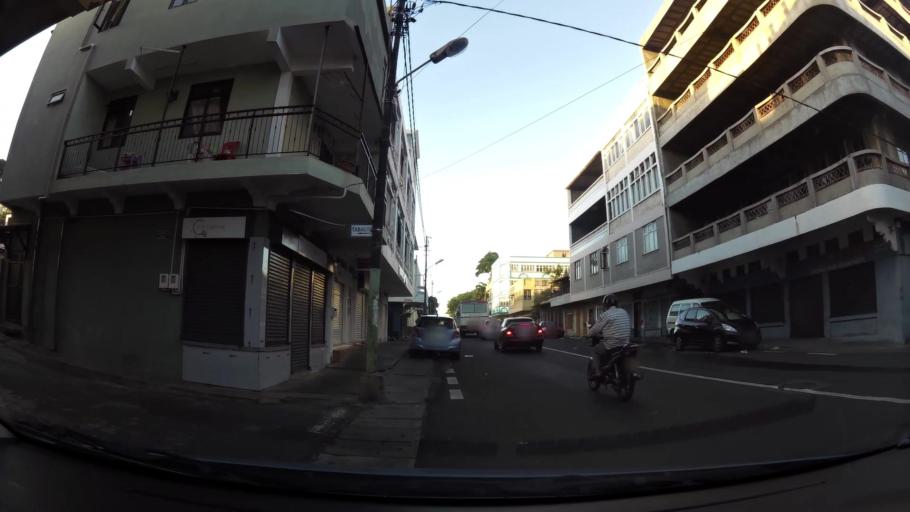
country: MU
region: Port Louis
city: Port Louis
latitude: -20.1548
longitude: 57.5104
